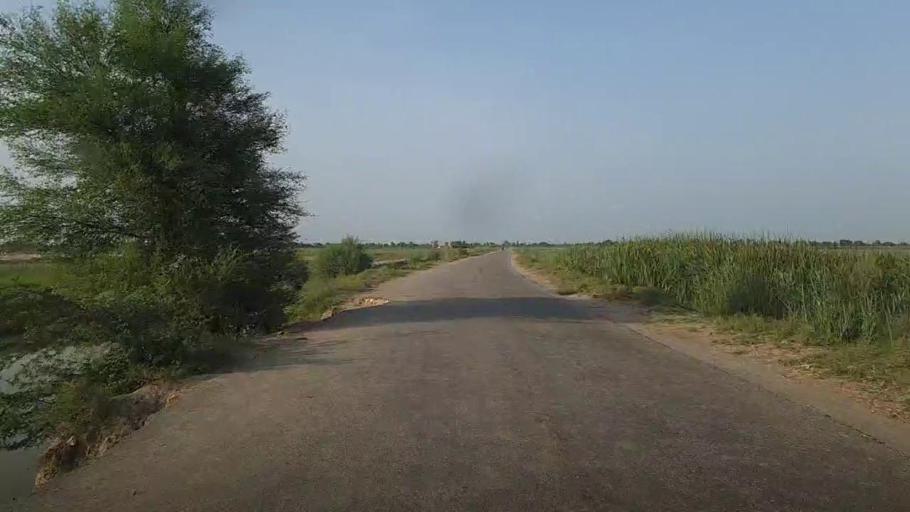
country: PK
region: Sindh
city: Khairpur
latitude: 28.0898
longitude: 69.8033
